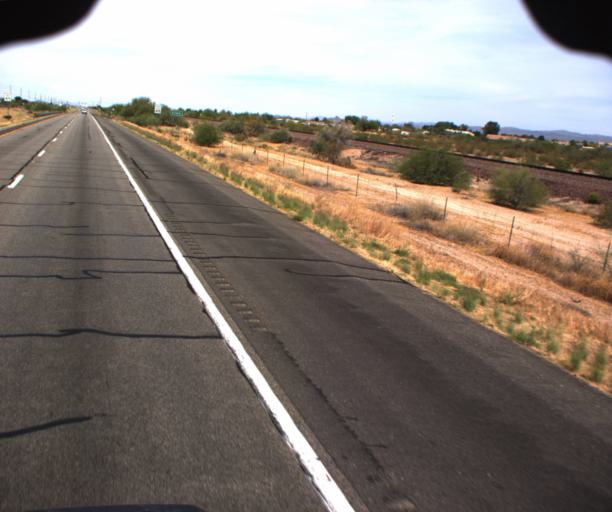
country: US
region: Arizona
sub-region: Maricopa County
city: Sun City West
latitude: 33.7738
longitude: -112.5232
